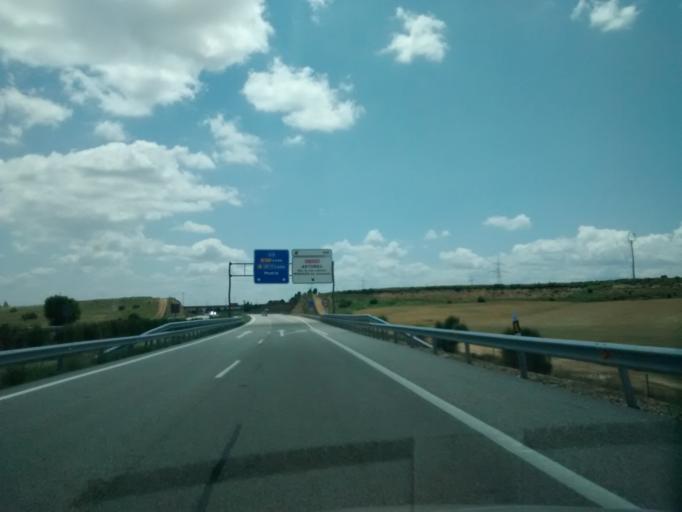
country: ES
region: Castille and Leon
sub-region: Provincia de Leon
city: Astorga
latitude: 42.4507
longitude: -6.0812
